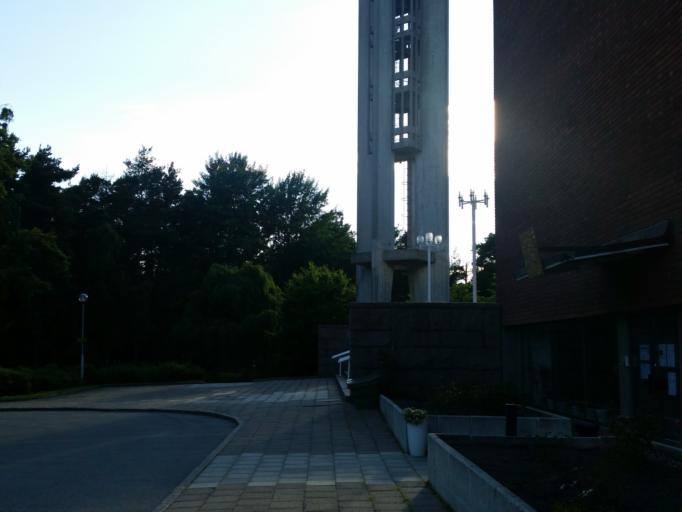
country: SE
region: Stockholm
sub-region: Solna Kommun
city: Rasunda
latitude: 59.3684
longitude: 17.9879
